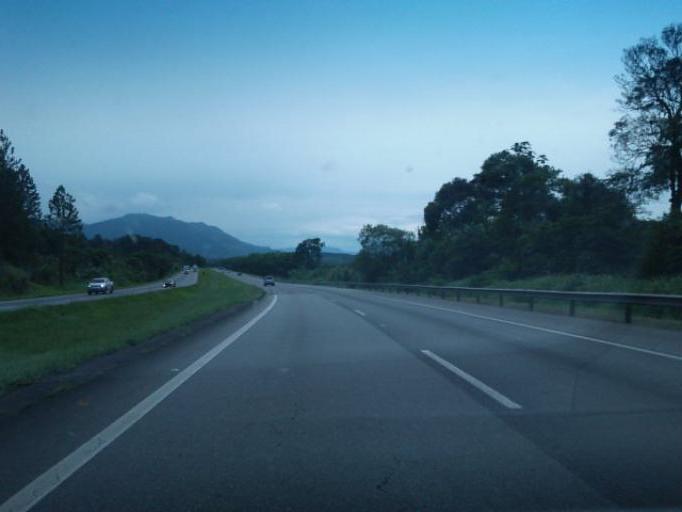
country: BR
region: Sao Paulo
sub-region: Jacupiranga
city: Jacupiranga
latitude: -24.7172
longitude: -48.0368
